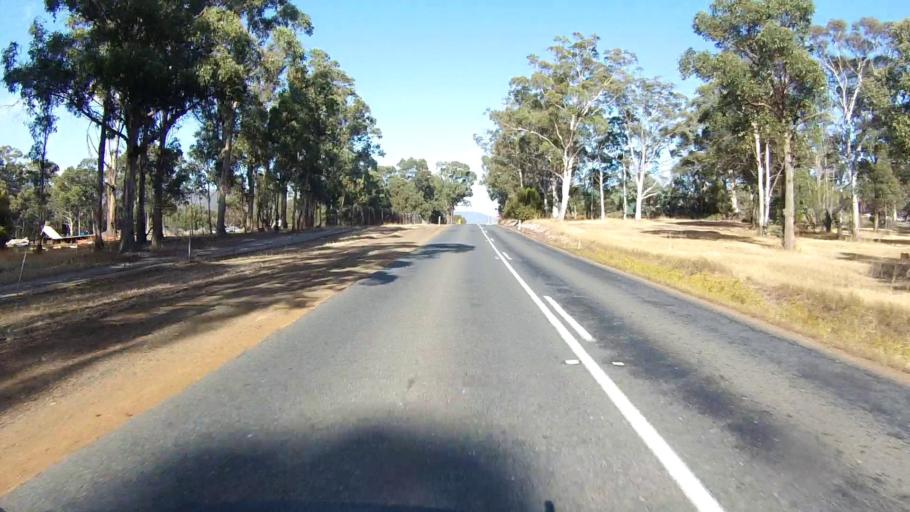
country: AU
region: Tasmania
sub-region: Derwent Valley
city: New Norfolk
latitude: -42.7763
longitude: 147.0989
